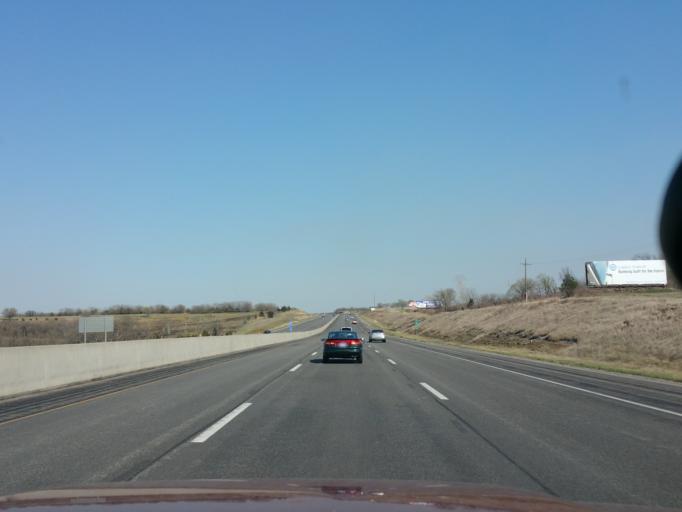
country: US
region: Kansas
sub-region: Douglas County
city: Lawrence
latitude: 39.0011
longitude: -95.4229
